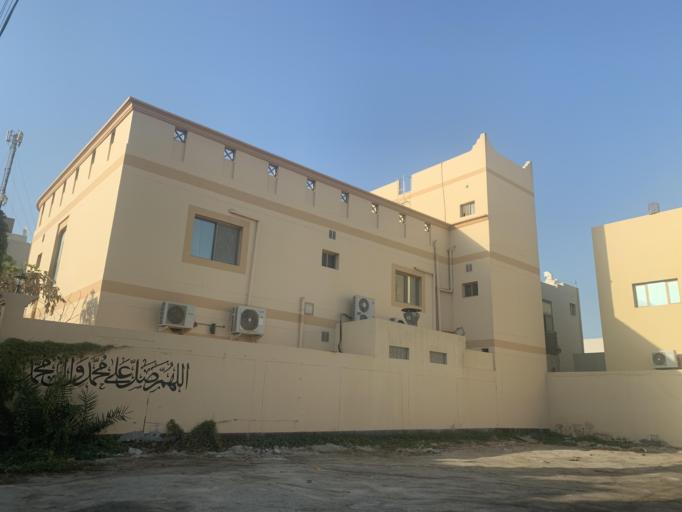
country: BH
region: Manama
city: Jidd Hafs
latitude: 26.2120
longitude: 50.5279
